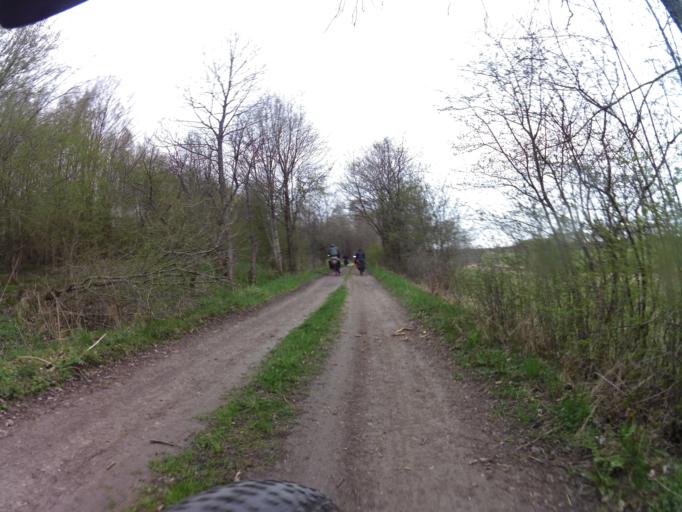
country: PL
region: West Pomeranian Voivodeship
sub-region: Powiat koszalinski
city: Bobolice
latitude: 54.0107
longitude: 16.6559
